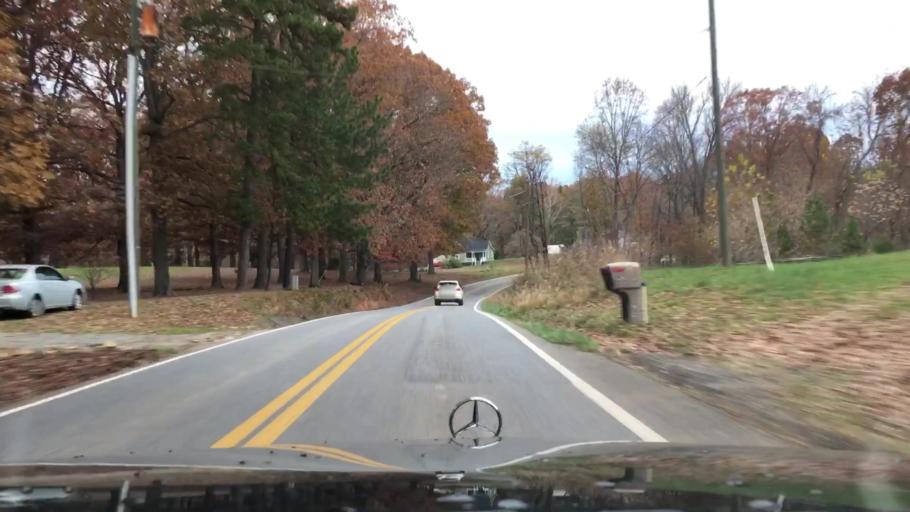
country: US
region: Virginia
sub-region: Campbell County
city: Timberlake
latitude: 37.2357
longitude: -79.2807
